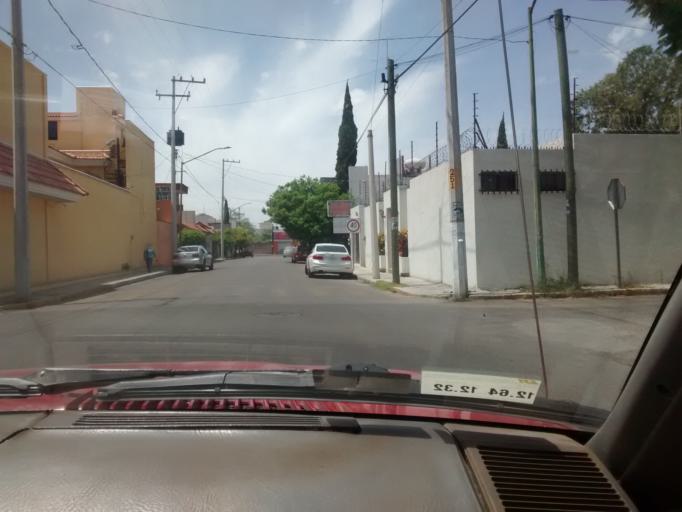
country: MX
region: Puebla
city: Tehuacan
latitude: 18.4615
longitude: -97.4112
